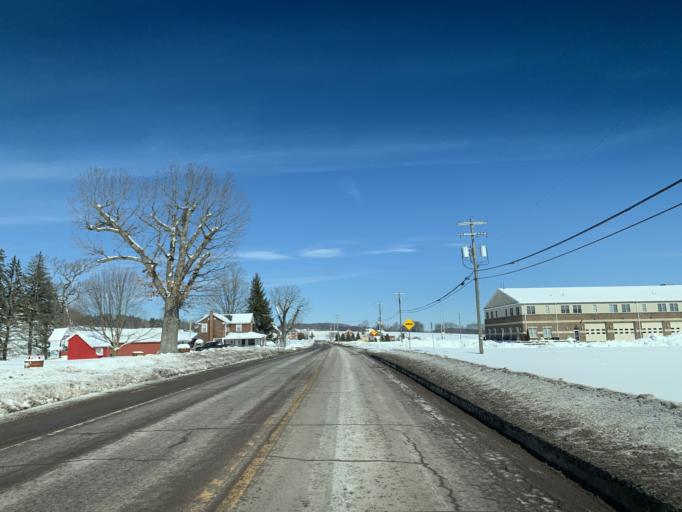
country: US
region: Pennsylvania
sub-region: Somerset County
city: Meyersdale
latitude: 39.7007
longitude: -79.1615
